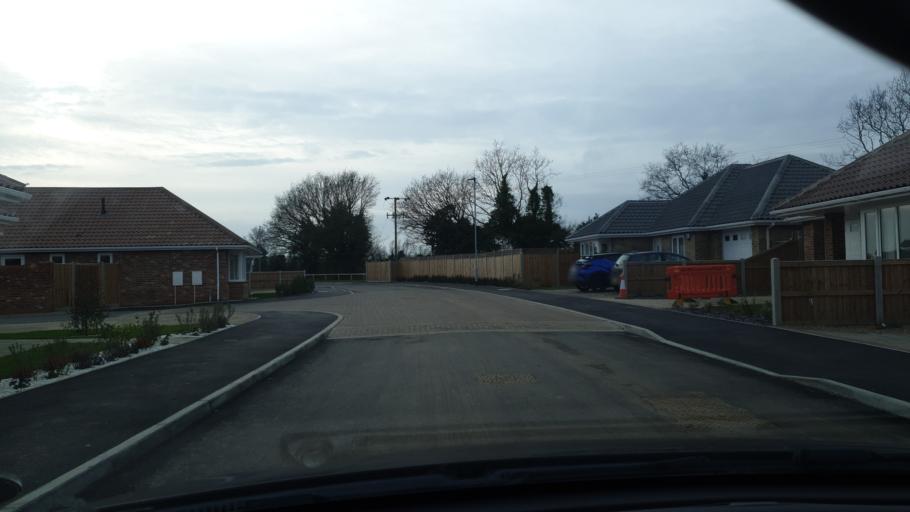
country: GB
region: England
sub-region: Essex
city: Great Bentley
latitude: 51.8429
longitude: 1.0338
